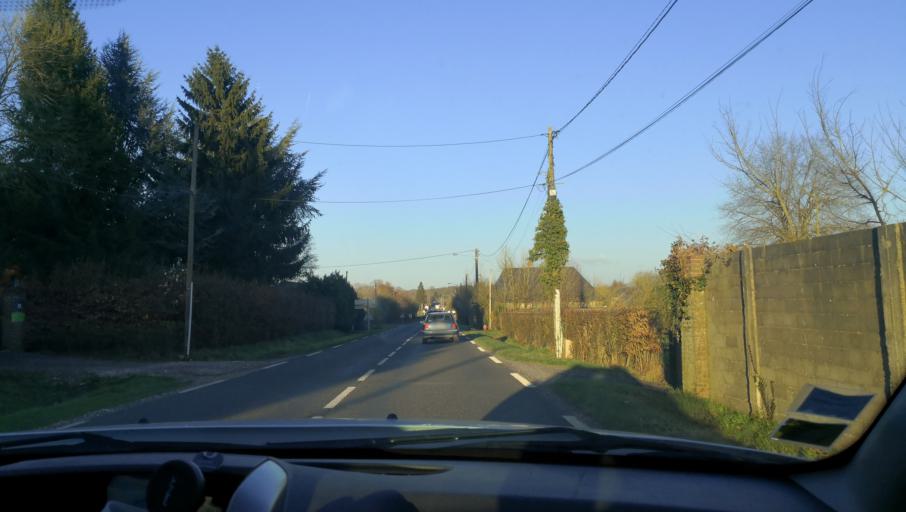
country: FR
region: Haute-Normandie
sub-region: Departement de la Seine-Maritime
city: Forges-les-Eaux
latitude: 49.6028
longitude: 1.4824
